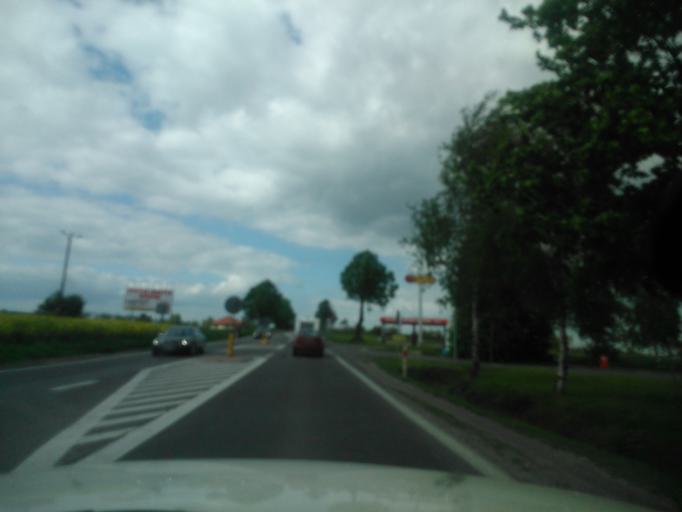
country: PL
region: Masovian Voivodeship
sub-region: Powiat radomski
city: Ilza
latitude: 51.1674
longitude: 21.2320
